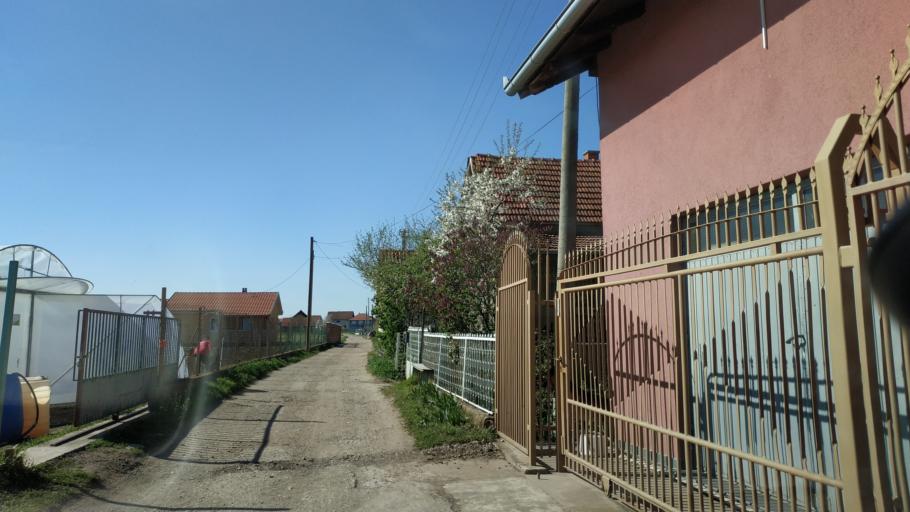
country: RS
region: Central Serbia
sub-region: Nisavski Okrug
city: Aleksinac
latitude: 43.4954
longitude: 21.6977
